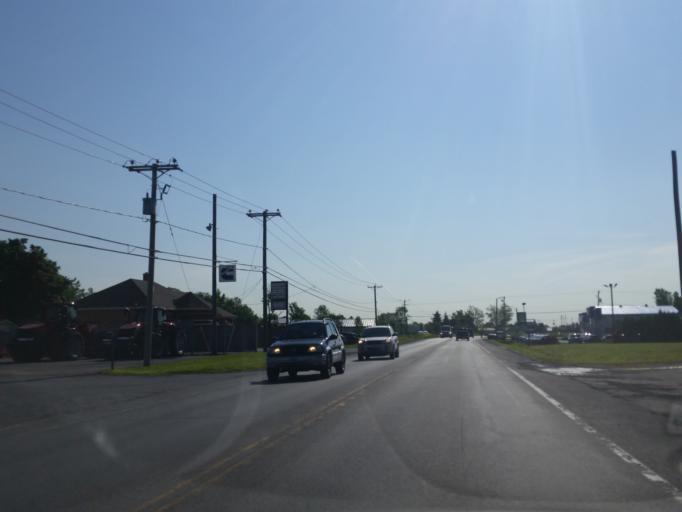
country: CA
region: Quebec
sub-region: Monteregie
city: Napierville
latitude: 45.1958
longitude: -73.4278
